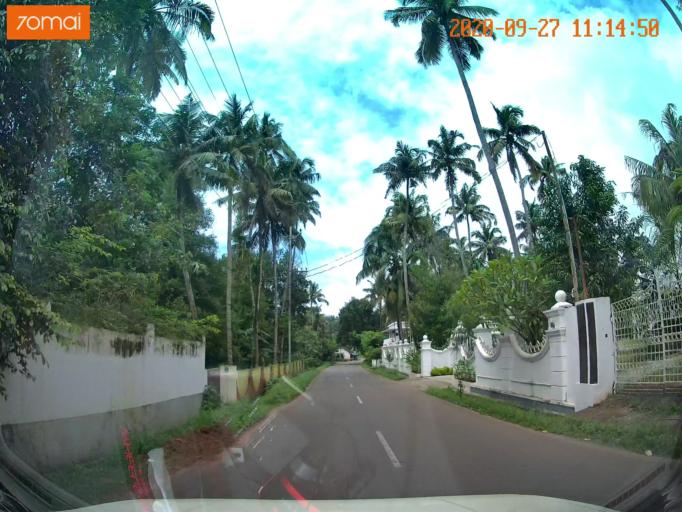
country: IN
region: Kerala
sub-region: Thrissur District
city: Thanniyam
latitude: 10.4313
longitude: 76.2032
